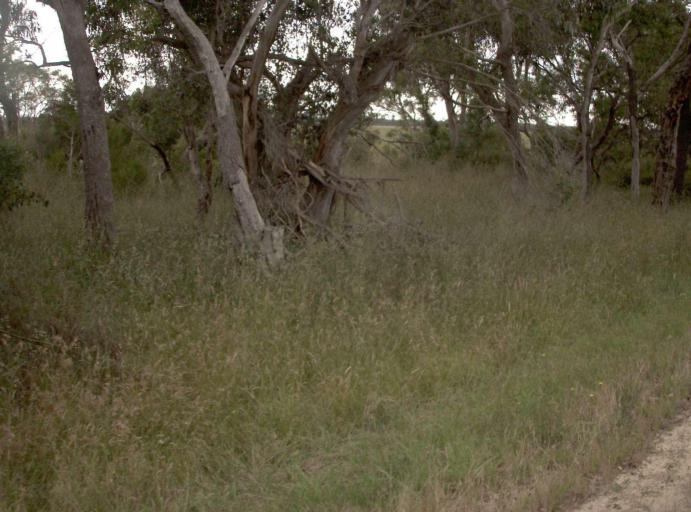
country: AU
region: Victoria
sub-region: Latrobe
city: Traralgon
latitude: -38.5546
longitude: 146.8152
